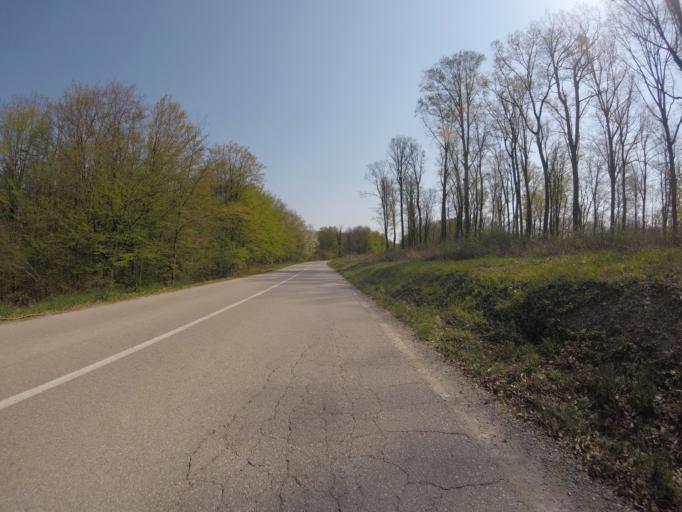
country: HR
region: Zagrebacka
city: Lukavec
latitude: 45.6378
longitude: 15.9614
